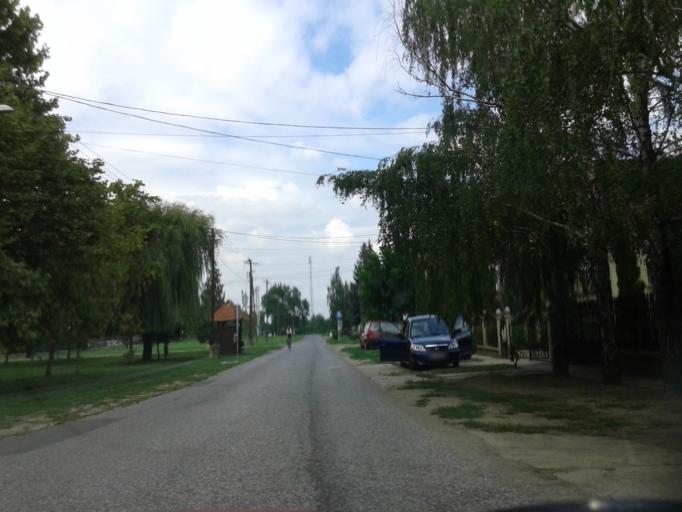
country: HU
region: Csongrad
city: Zakanyszek
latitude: 46.2769
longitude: 19.8856
